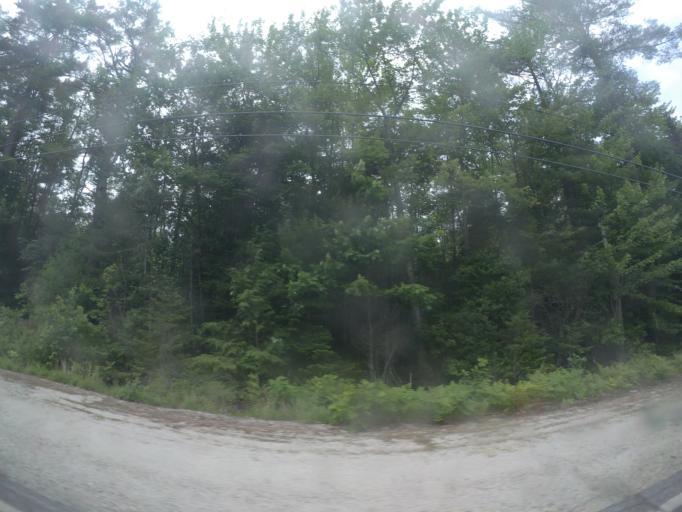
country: US
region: Maine
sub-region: Cumberland County
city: Falmouth
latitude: 43.7549
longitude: -70.2420
